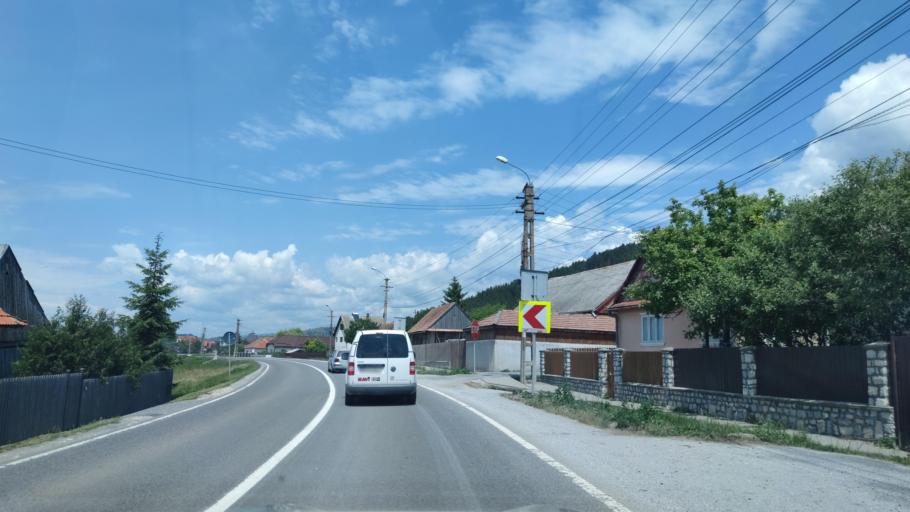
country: RO
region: Harghita
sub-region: Comuna Voslobeni
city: Voslobeni
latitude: 46.6385
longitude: 25.6251
